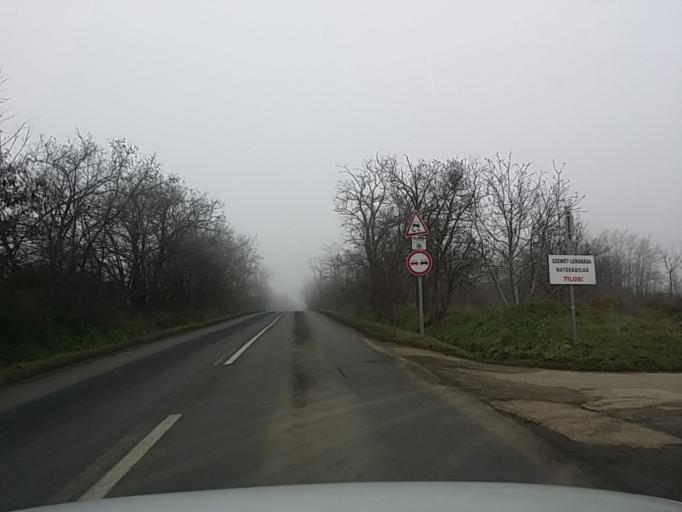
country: HU
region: Pest
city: Budakeszi
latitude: 47.5165
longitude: 18.9172
